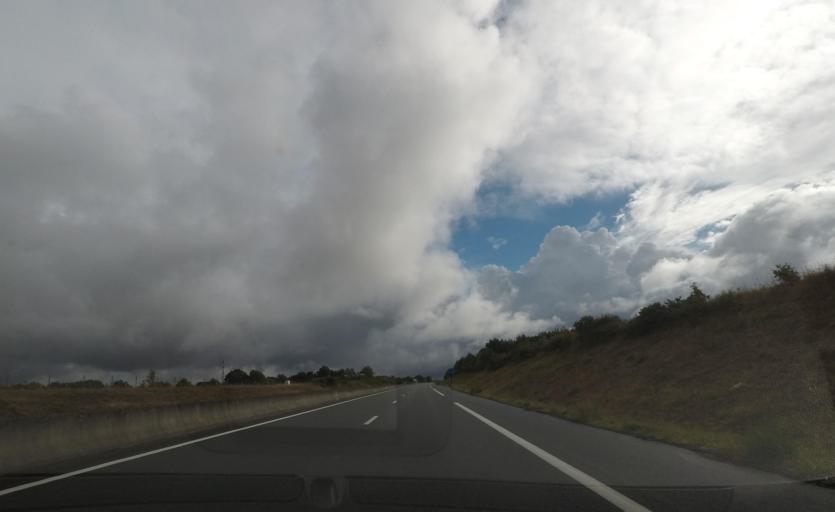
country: FR
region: Pays de la Loire
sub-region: Departement de la Vendee
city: La Roche-sur-Yon
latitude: 46.6535
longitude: -1.3839
